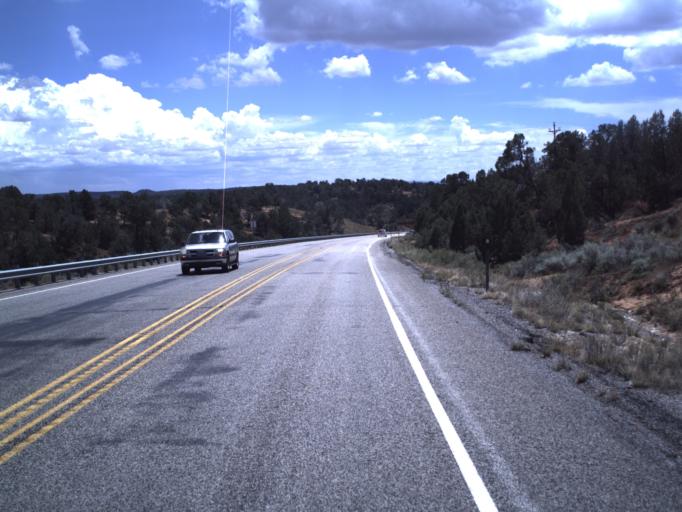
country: US
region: Utah
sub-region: Kane County
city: Kanab
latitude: 37.1491
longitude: -112.5701
